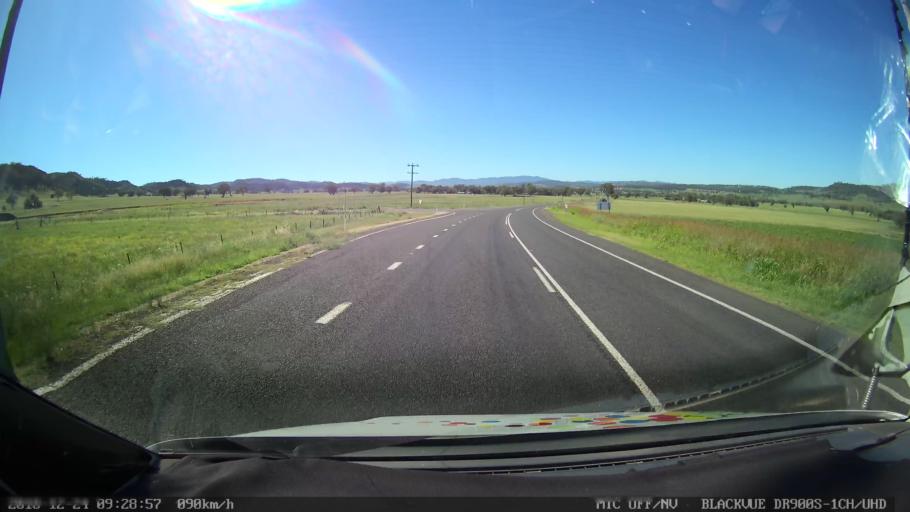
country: AU
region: New South Wales
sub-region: Liverpool Plains
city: Quirindi
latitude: -31.5436
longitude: 150.6925
